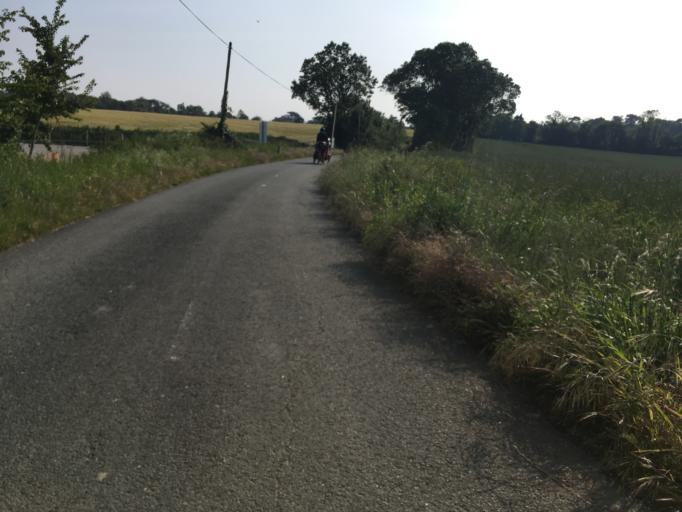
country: FR
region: Poitou-Charentes
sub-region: Departement de la Charente-Maritime
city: Lagord
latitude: 46.1817
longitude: -1.1803
